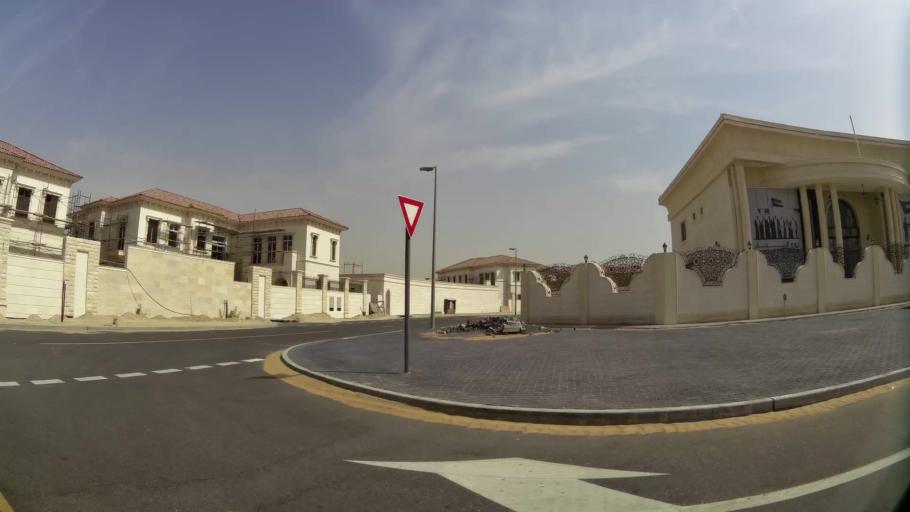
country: AE
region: Ash Shariqah
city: Sharjah
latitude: 25.2645
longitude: 55.4704
